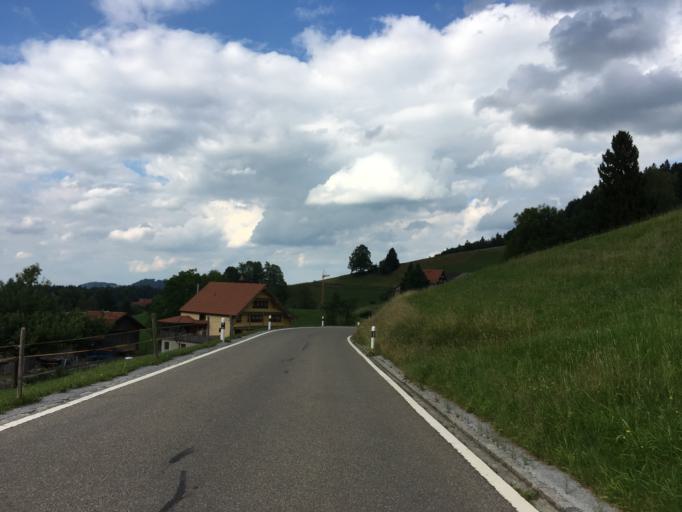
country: CH
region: Saint Gallen
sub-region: Wahlkreis Toggenburg
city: Lichtensteig
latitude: 47.3208
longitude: 9.0634
